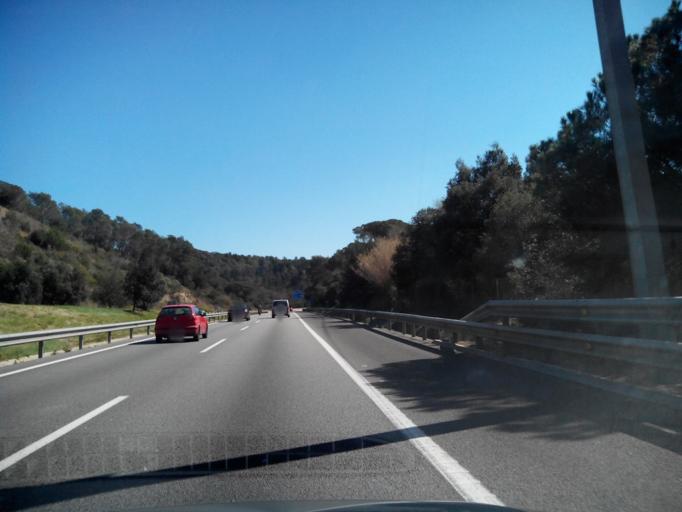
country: ES
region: Catalonia
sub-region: Provincia de Barcelona
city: La Roca del Valles
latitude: 41.5856
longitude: 2.3544
